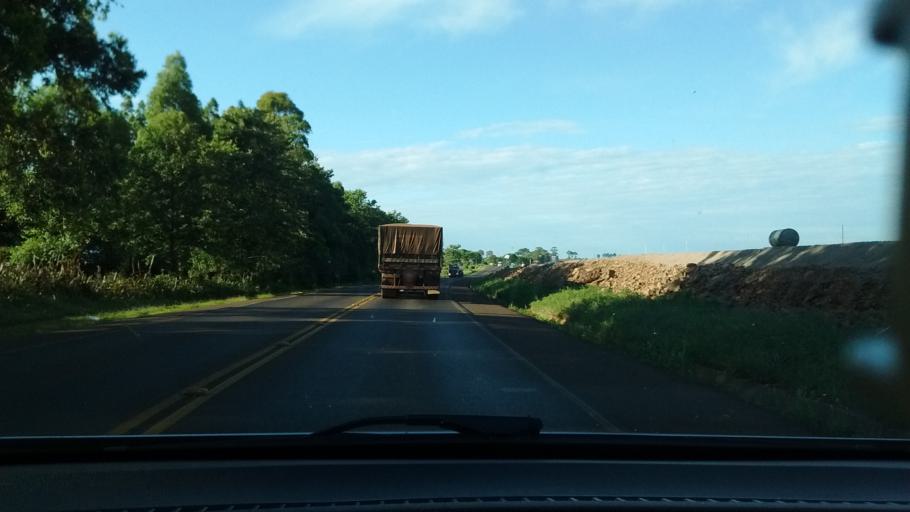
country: BR
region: Parana
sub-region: Cascavel
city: Cascavel
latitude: -25.1639
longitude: -53.5981
